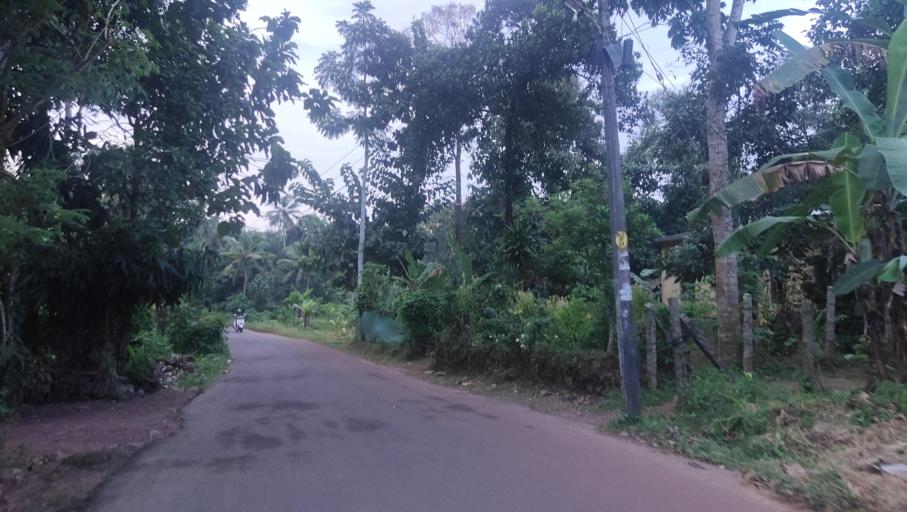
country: IN
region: Kerala
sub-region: Alappuzha
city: Kattanam
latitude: 9.1327
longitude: 76.6353
